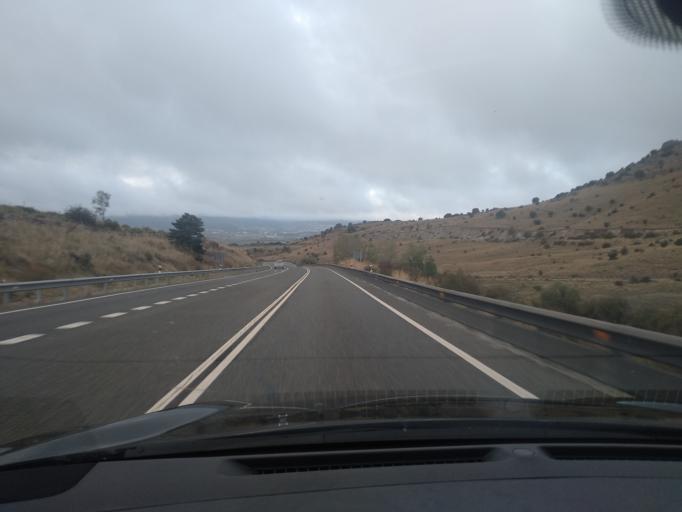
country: ES
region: Castille and Leon
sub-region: Provincia de Segovia
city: Otero de Herreros
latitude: 40.7645
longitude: -4.2083
